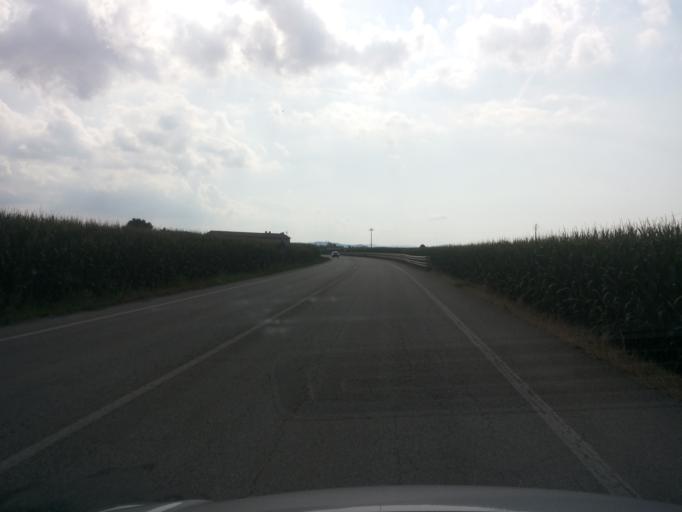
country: IT
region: Piedmont
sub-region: Provincia di Alessandria
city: Villanova Monferrato
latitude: 45.1611
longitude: 8.4702
